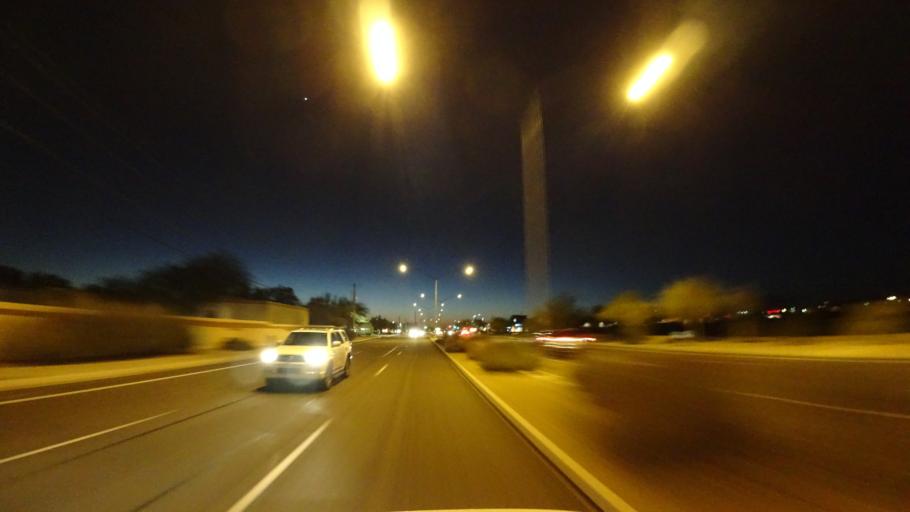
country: US
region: Arizona
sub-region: Pinal County
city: Apache Junction
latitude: 33.4514
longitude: -111.6799
